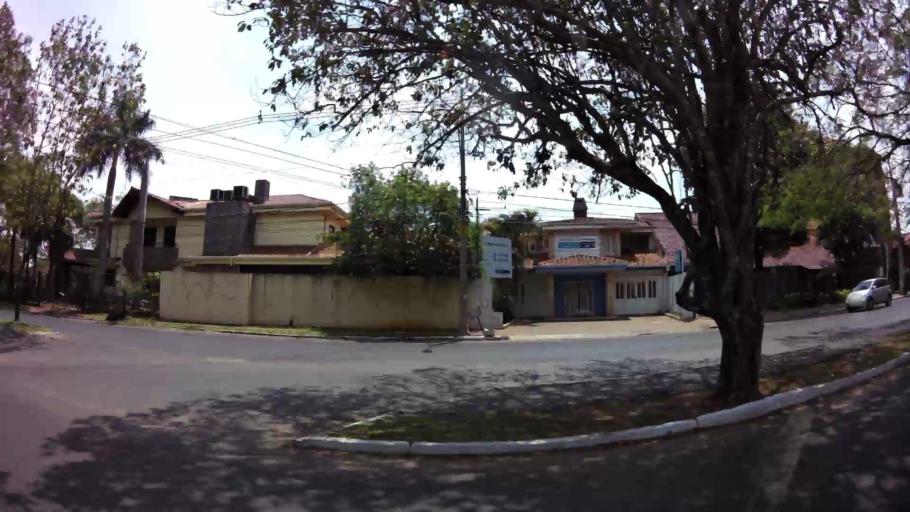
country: PY
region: Central
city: Lambare
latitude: -25.2990
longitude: -57.5734
